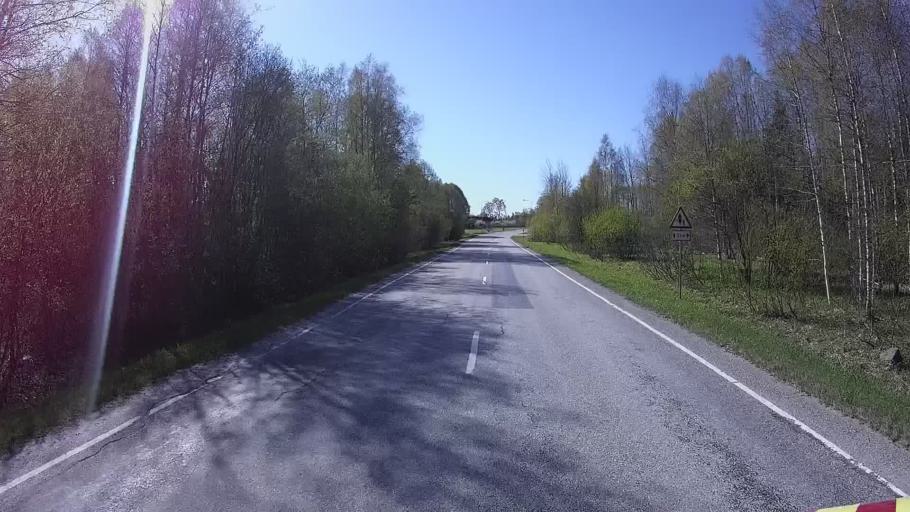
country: EE
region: Raplamaa
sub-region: Jaervakandi vald
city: Jarvakandi
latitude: 58.7943
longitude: 24.8179
